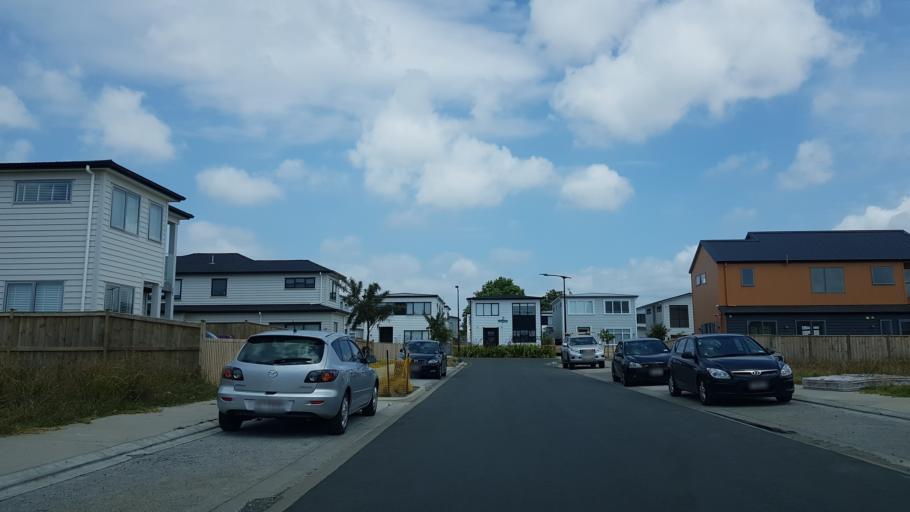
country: NZ
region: Auckland
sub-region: Auckland
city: Rosebank
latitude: -36.8037
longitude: 174.6637
